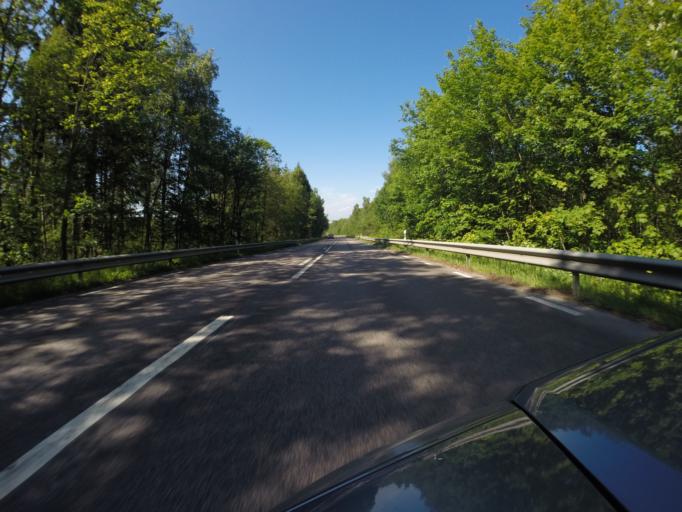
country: SE
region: Skane
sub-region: Bjuvs Kommun
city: Billesholm
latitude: 56.0362
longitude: 12.9697
